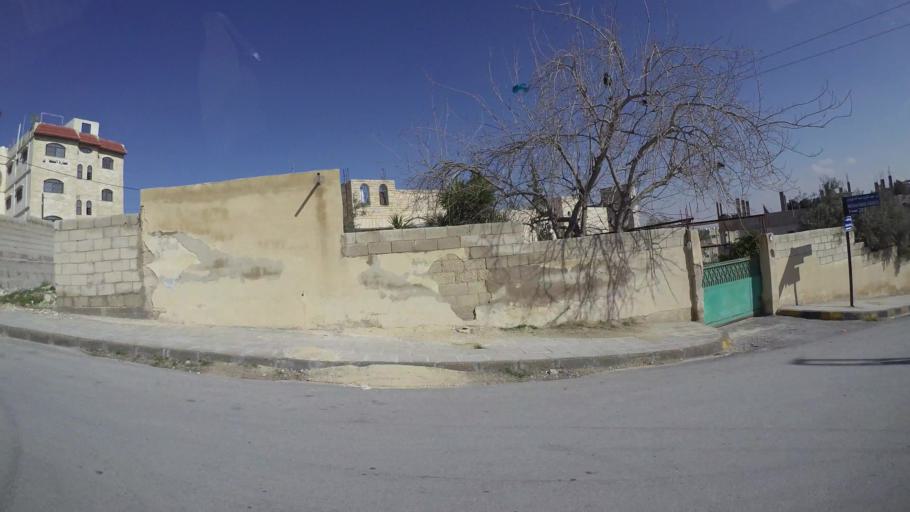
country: JO
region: Zarqa
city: Russeifa
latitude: 32.0375
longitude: 36.0327
